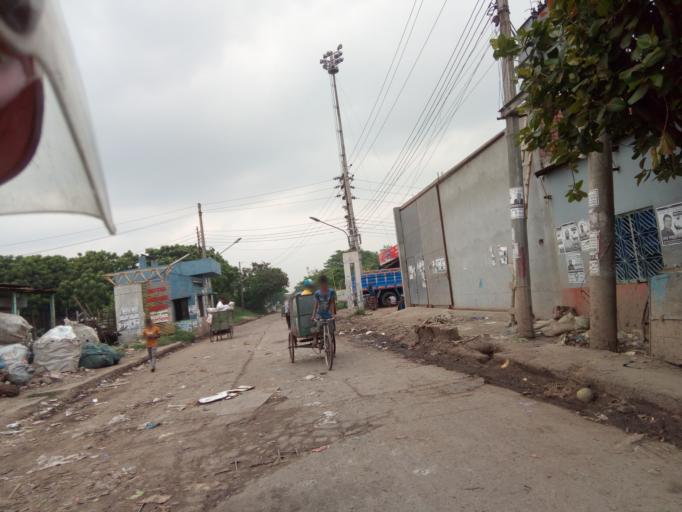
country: BD
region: Dhaka
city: Paltan
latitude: 23.7154
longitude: 90.4504
